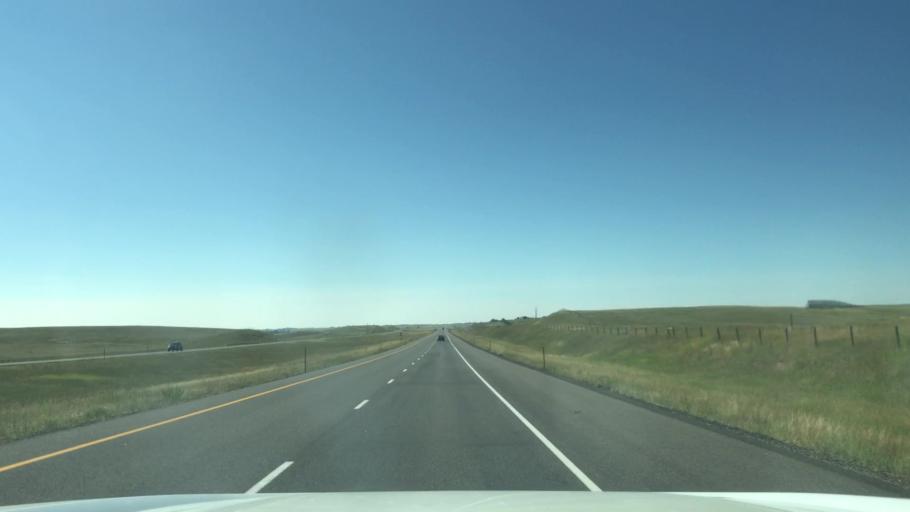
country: US
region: Wyoming
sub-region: Laramie County
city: Ranchettes
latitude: 41.2702
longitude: -104.8444
